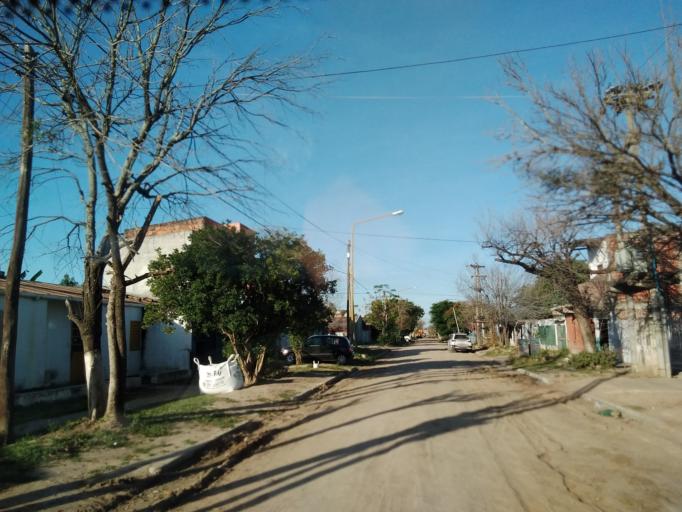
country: AR
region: Corrientes
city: Corrientes
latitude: -27.5043
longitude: -58.8341
